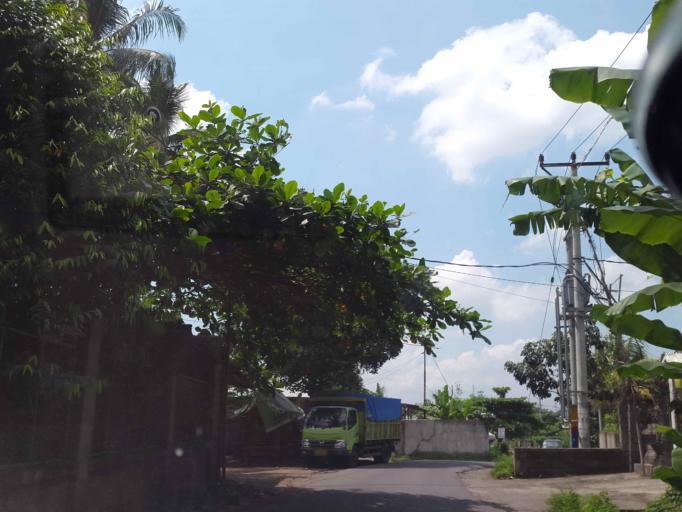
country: ID
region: West Nusa Tenggara
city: Mambalan
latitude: -8.5457
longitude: 116.1129
